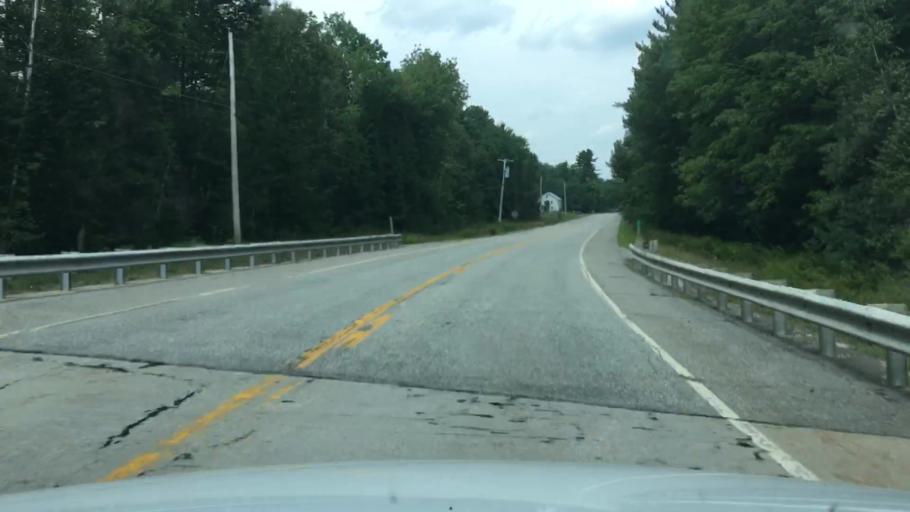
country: US
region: Maine
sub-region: Oxford County
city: Rumford
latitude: 44.5594
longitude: -70.7158
